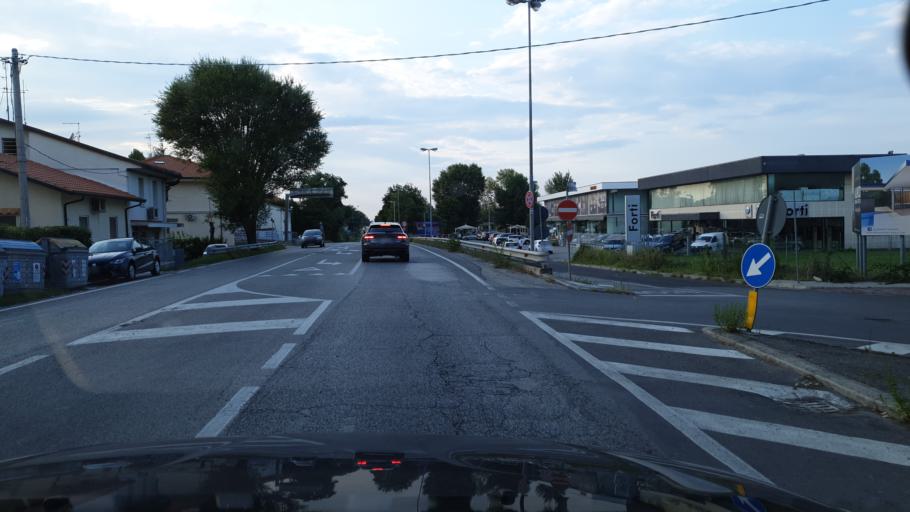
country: IT
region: Emilia-Romagna
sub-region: Provincia di Rimini
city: Rivazzurra
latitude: 44.0188
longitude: 12.6274
